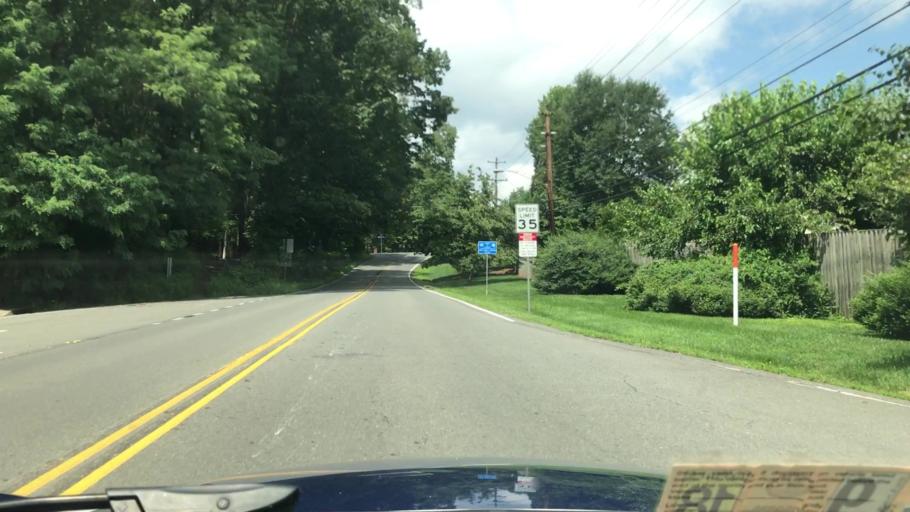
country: US
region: Virginia
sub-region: Fairfax County
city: Vienna
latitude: 38.9067
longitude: -77.2801
